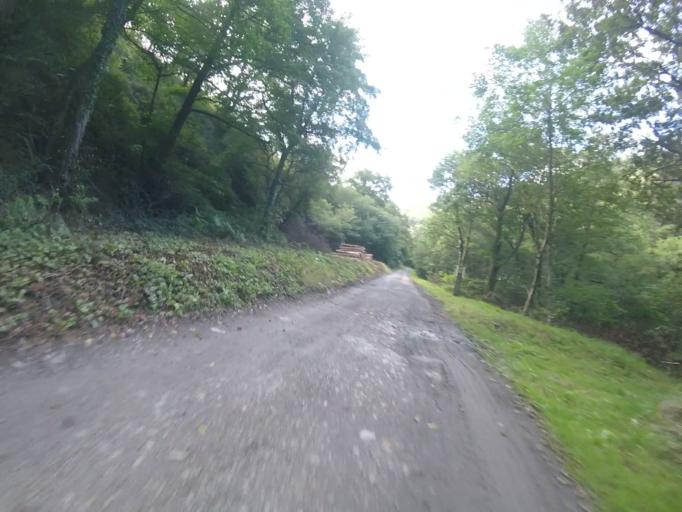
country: ES
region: Basque Country
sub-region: Provincia de Guipuzcoa
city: Berastegui
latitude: 43.1298
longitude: -1.9389
